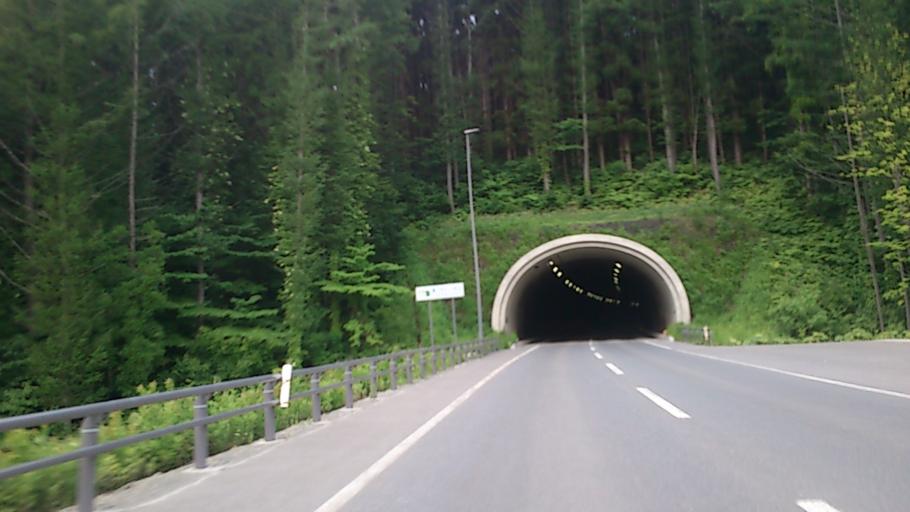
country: JP
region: Aomori
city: Hirosaki
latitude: 40.5317
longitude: 140.2478
